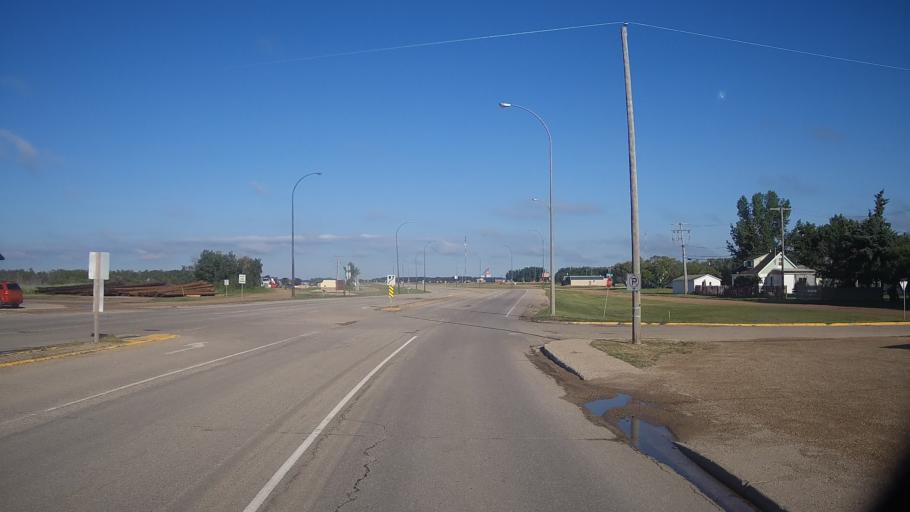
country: CA
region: Saskatchewan
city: Lanigan
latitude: 51.8462
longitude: -105.0377
